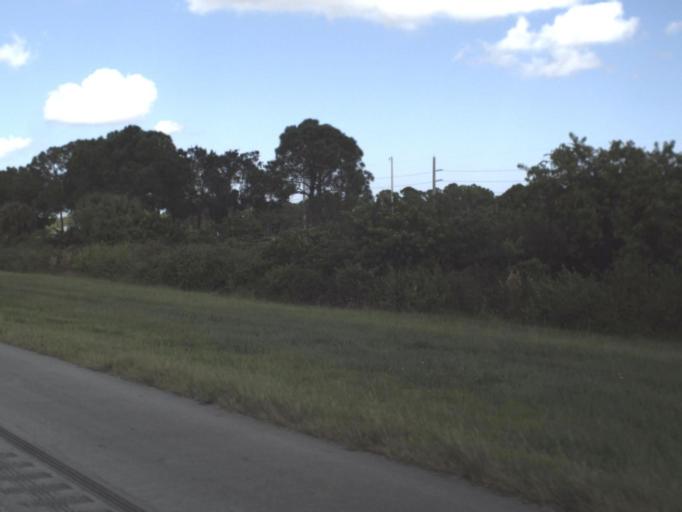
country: US
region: Florida
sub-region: Martin County
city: Port Salerno
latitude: 27.0901
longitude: -80.2549
